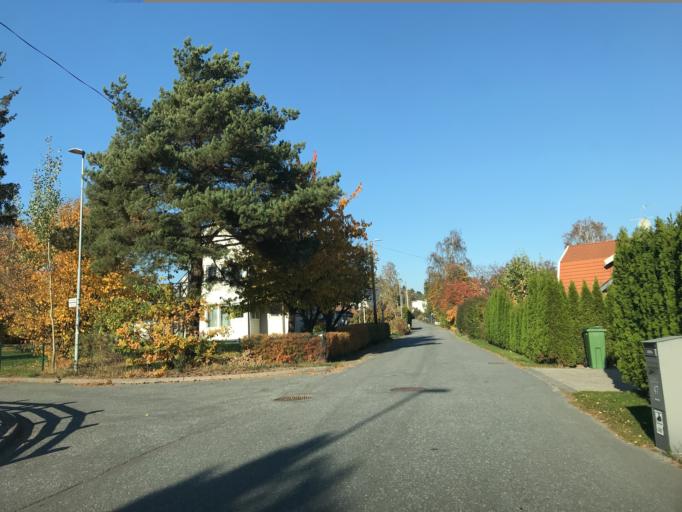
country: SE
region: Stockholm
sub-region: Sollentuna Kommun
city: Sollentuna
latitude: 59.4203
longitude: 17.9371
